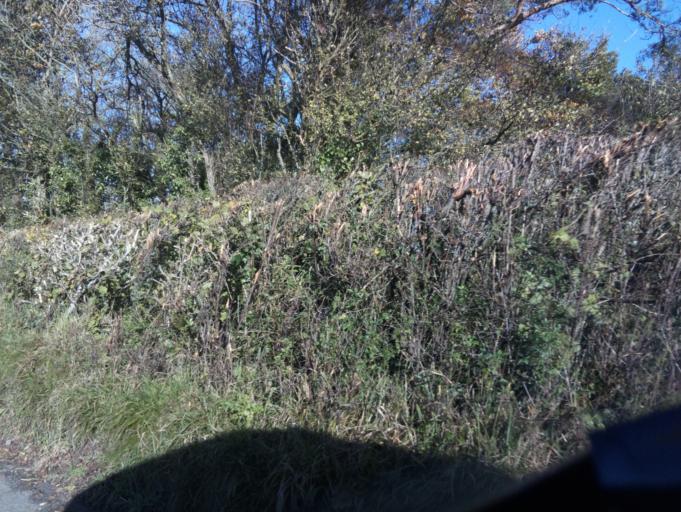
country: GB
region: England
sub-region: Somerset
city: Yeovil
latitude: 50.8940
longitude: -2.5971
